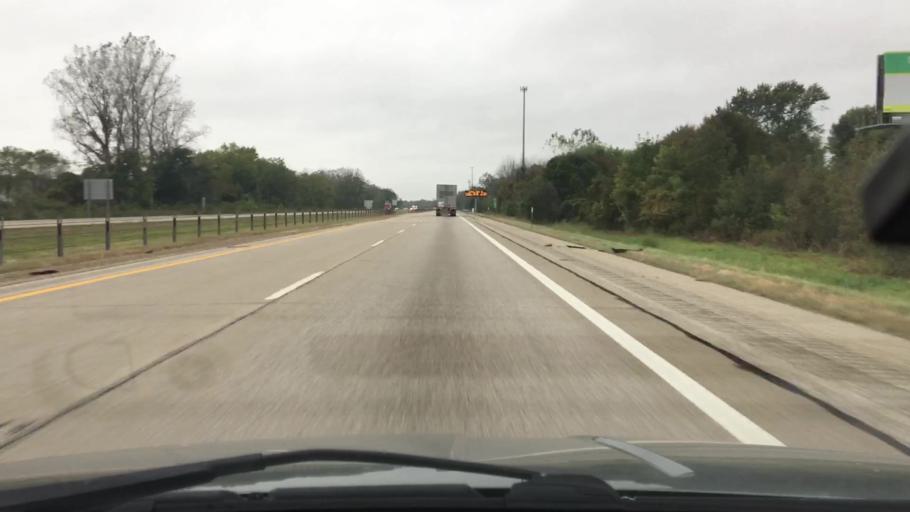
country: US
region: Michigan
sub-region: Van Buren County
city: Hartford
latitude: 42.1907
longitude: -86.1838
